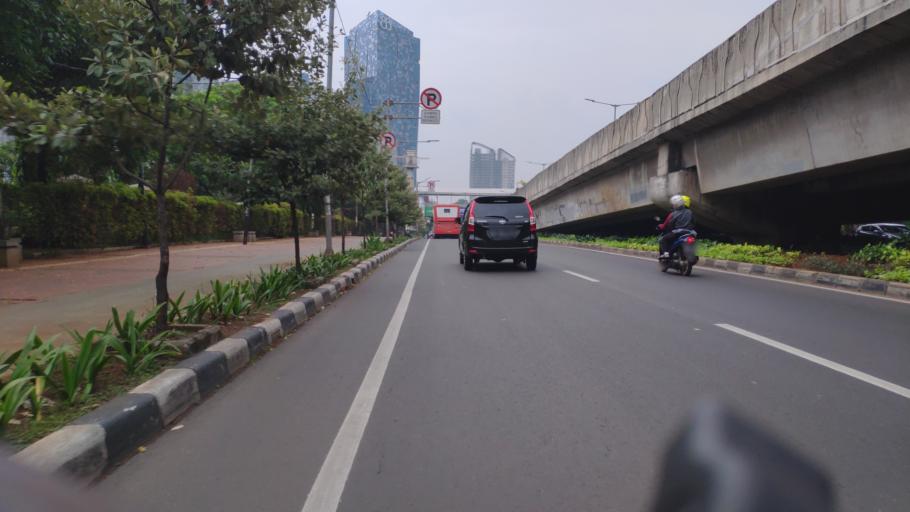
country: ID
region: Jakarta Raya
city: Jakarta
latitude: -6.2253
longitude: 106.8369
